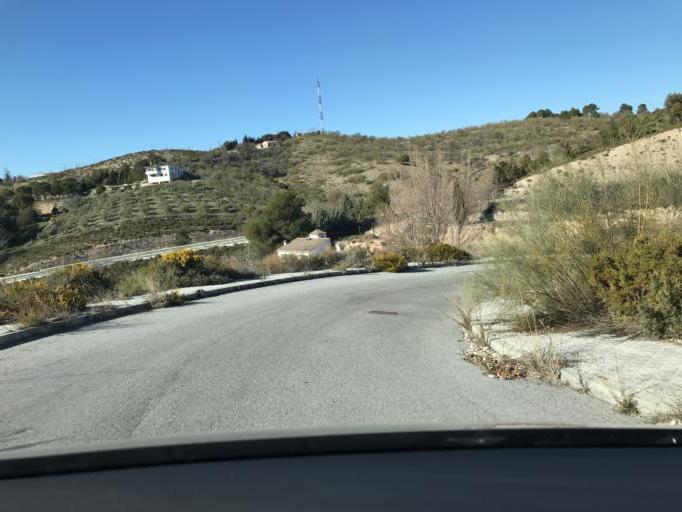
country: ES
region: Andalusia
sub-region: Provincia de Granada
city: Viznar
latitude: 37.2181
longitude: -3.5412
